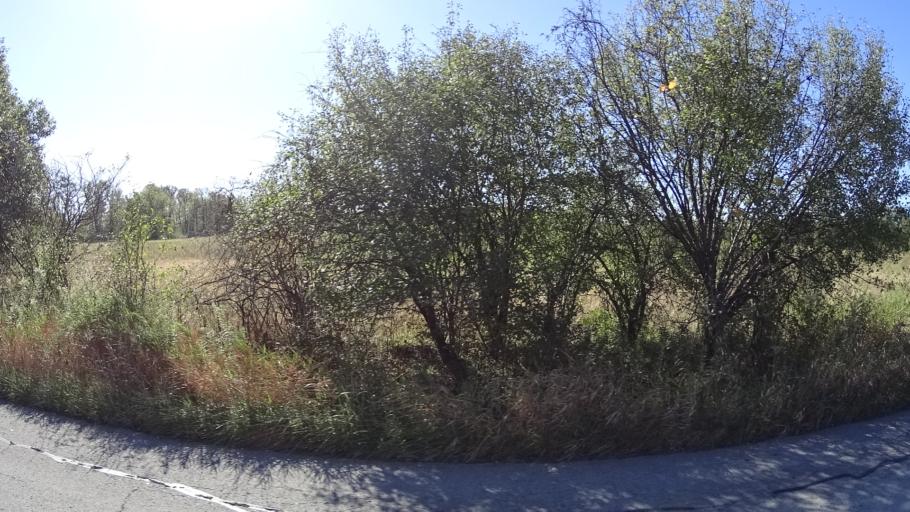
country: US
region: Ohio
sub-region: Lorain County
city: Oberlin
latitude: 41.2797
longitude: -82.2330
